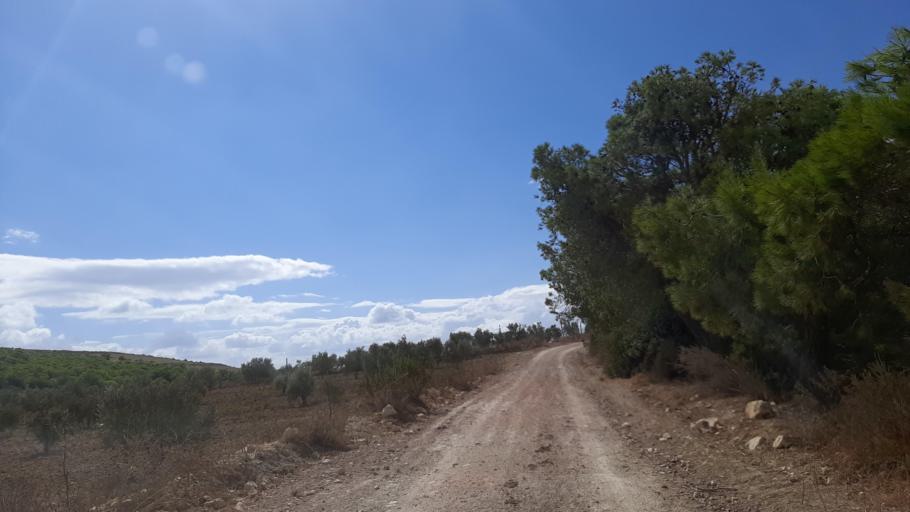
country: TN
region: Zaghwan
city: Zaghouan
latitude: 36.5122
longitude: 10.1834
